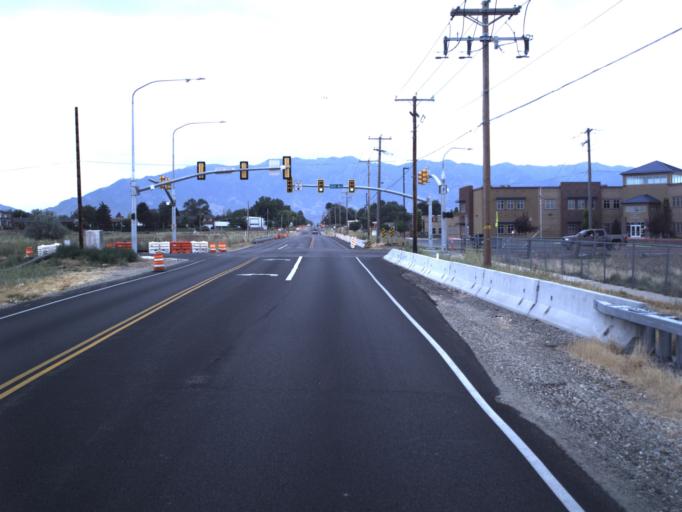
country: US
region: Utah
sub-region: Davis County
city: Syracuse
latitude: 41.0892
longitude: -112.0848
